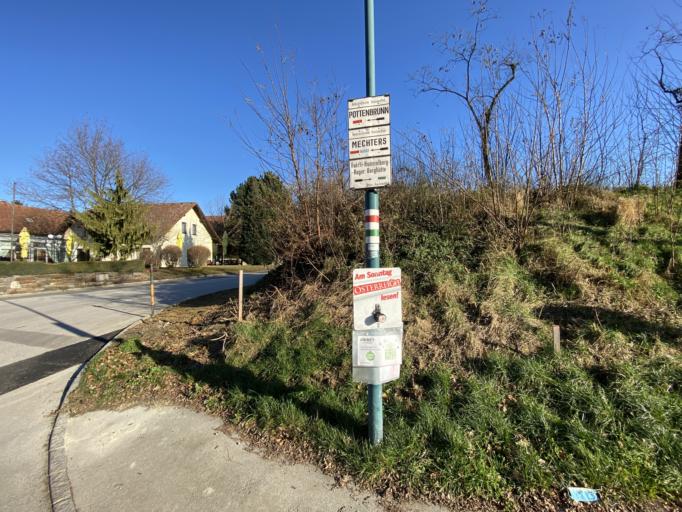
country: AT
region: Lower Austria
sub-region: Politischer Bezirk Sankt Polten
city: Boheimkirchen
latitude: 48.2001
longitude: 15.7544
